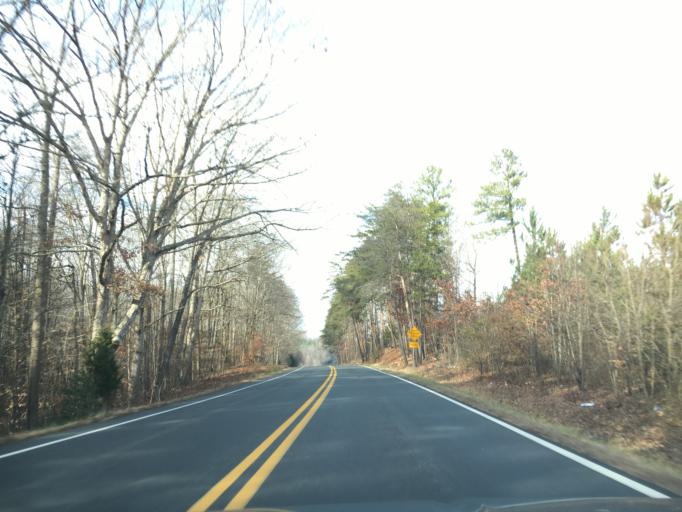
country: US
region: Virginia
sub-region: Louisa County
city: Louisa
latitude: 38.0951
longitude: -77.8901
